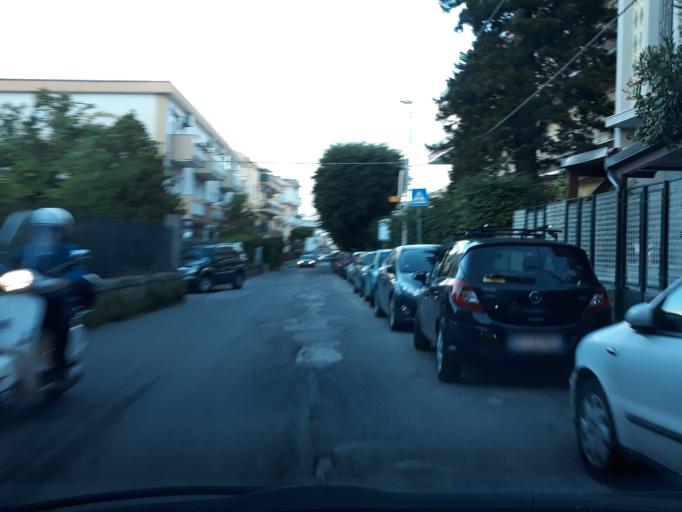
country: IT
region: Sicily
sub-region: Palermo
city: Villa Ciambra
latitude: 38.0880
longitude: 13.3293
